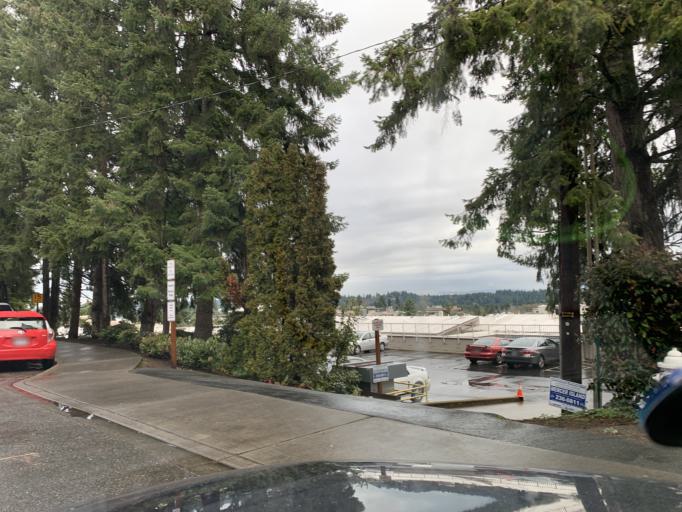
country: US
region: Washington
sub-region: King County
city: Mercer Island
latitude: 47.5831
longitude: -122.2378
